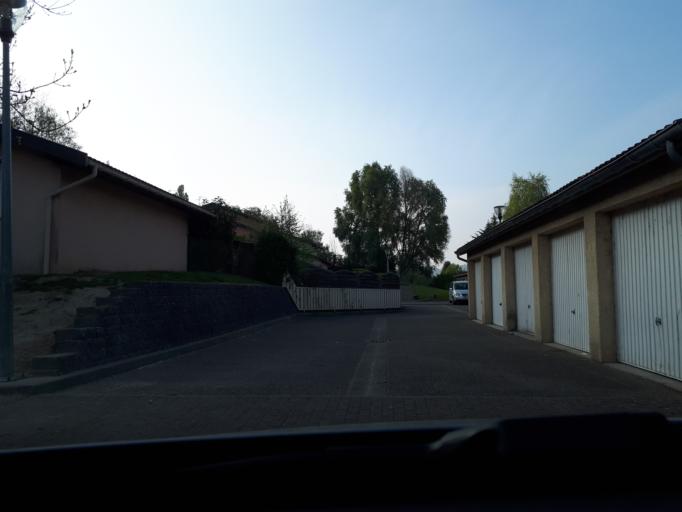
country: FR
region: Rhone-Alpes
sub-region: Departement de l'Isere
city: Bourgoin-Jallieu
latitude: 45.6050
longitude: 5.2734
